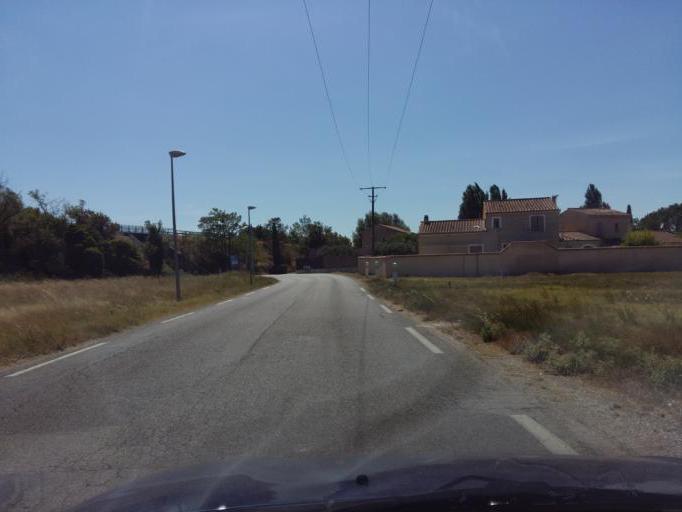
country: FR
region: Provence-Alpes-Cote d'Azur
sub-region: Departement du Vaucluse
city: Sarrians
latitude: 44.0873
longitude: 4.9816
